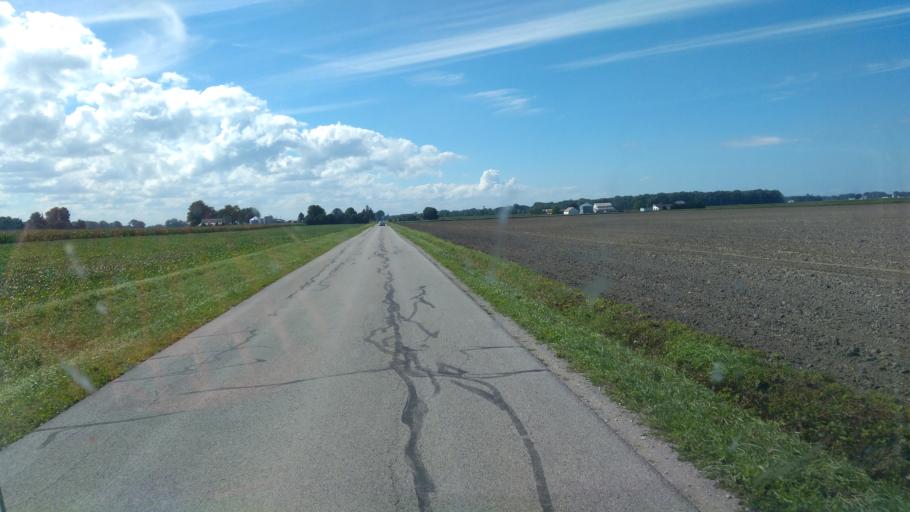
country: US
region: Ohio
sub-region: Ottawa County
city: Port Clinton
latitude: 41.4083
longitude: -82.8551
